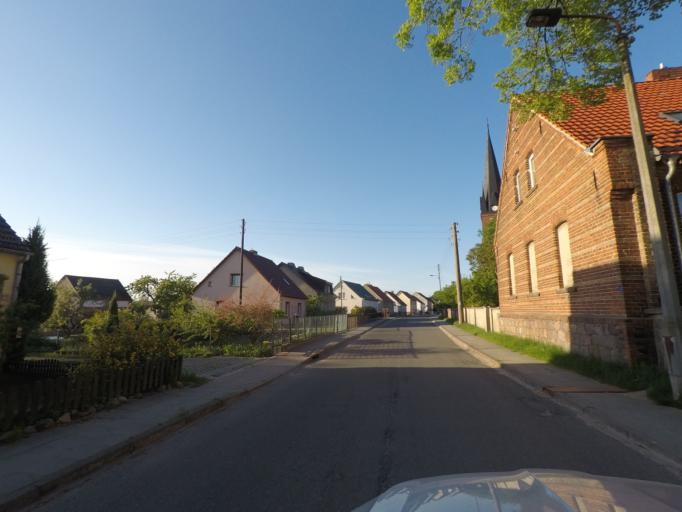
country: DE
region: Brandenburg
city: Liepe
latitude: 52.8355
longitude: 14.0059
